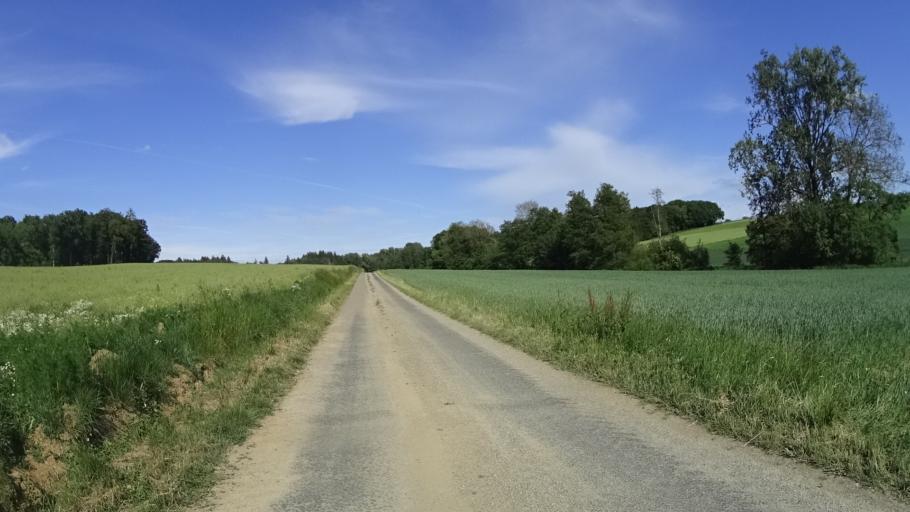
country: DE
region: Baden-Wuerttemberg
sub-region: Regierungsbezirk Stuttgart
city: Buch am Ahorn
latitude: 49.5270
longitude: 9.5335
